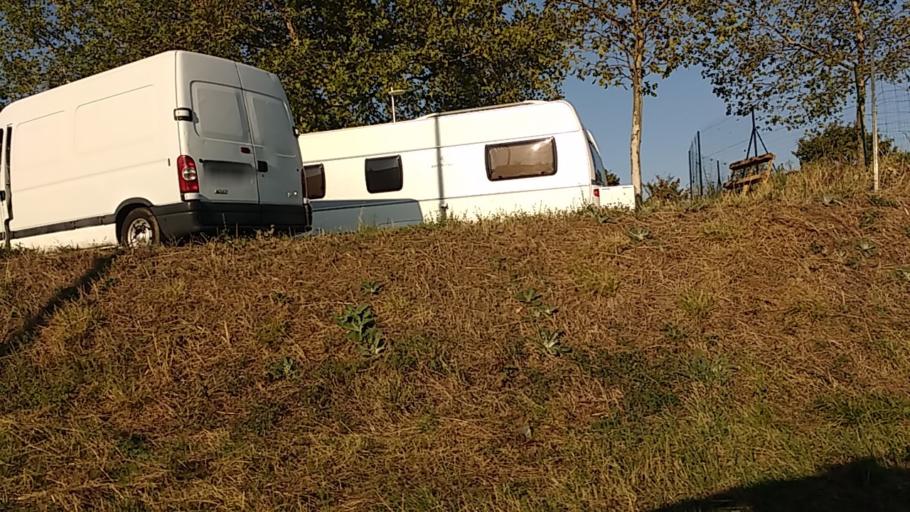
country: FR
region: Midi-Pyrenees
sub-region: Departement de la Haute-Garonne
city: Cugnaux
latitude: 43.5689
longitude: 1.3757
